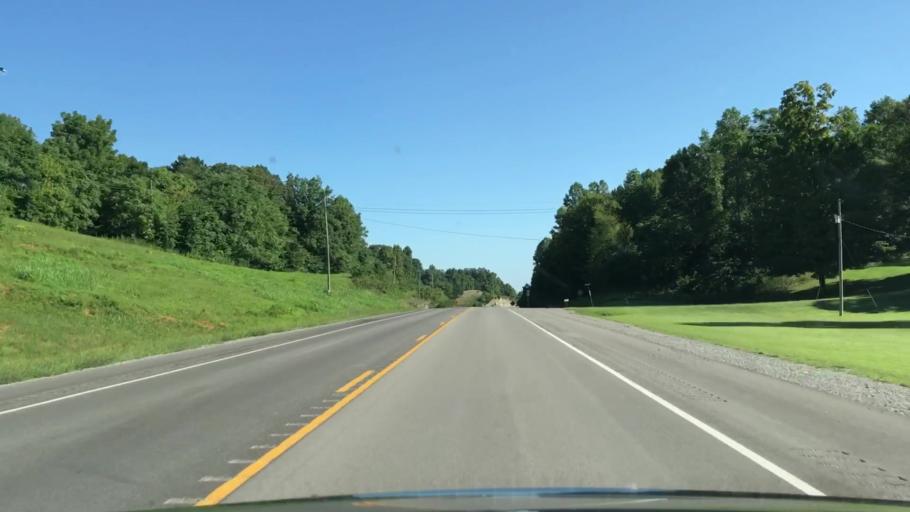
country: US
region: Kentucky
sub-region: Cumberland County
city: Burkesville
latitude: 36.6997
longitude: -85.3724
